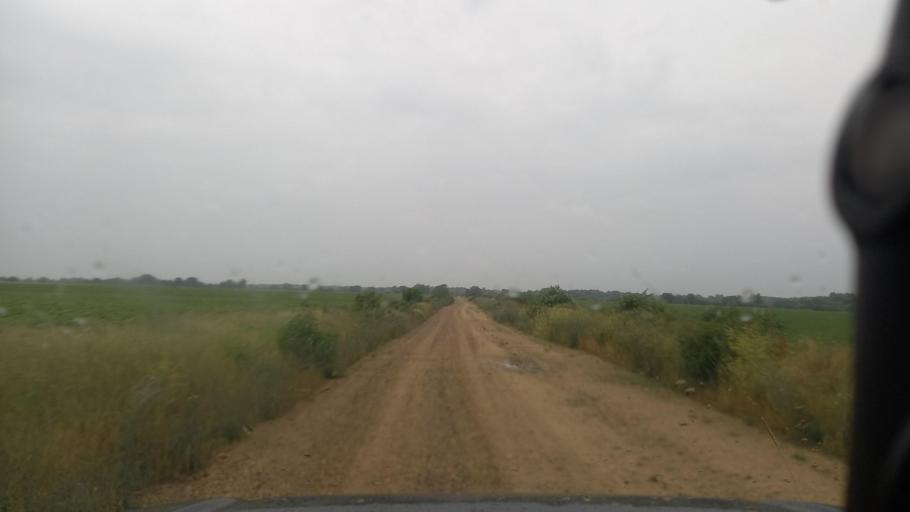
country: RU
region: Krasnodarskiy
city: Vasyurinskaya
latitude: 45.0218
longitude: 39.4886
